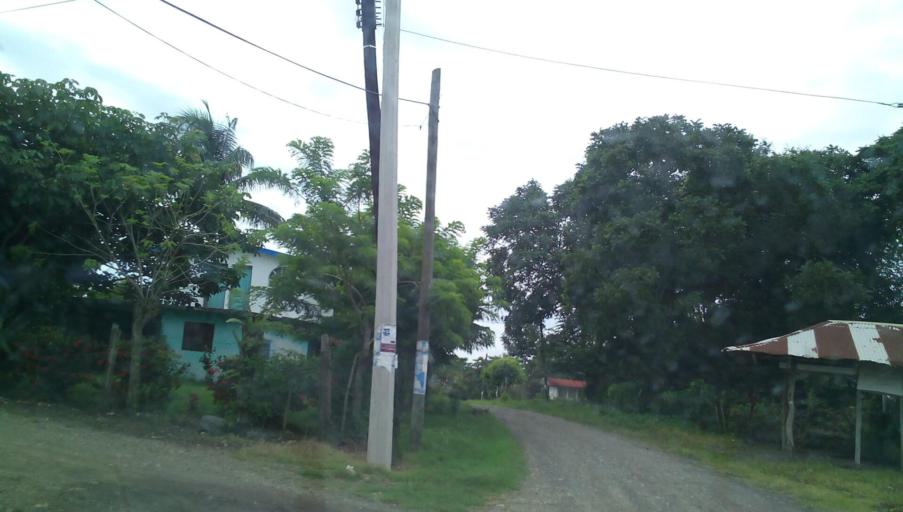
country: MX
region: Veracruz
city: Tepetzintla
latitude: 21.1268
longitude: -97.8542
